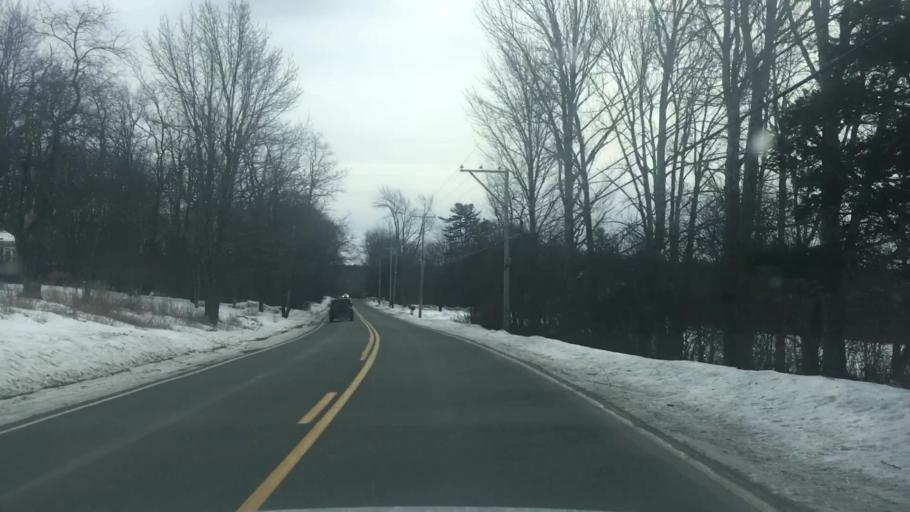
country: US
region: Maine
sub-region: Hancock County
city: Orland
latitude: 44.5627
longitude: -68.7396
